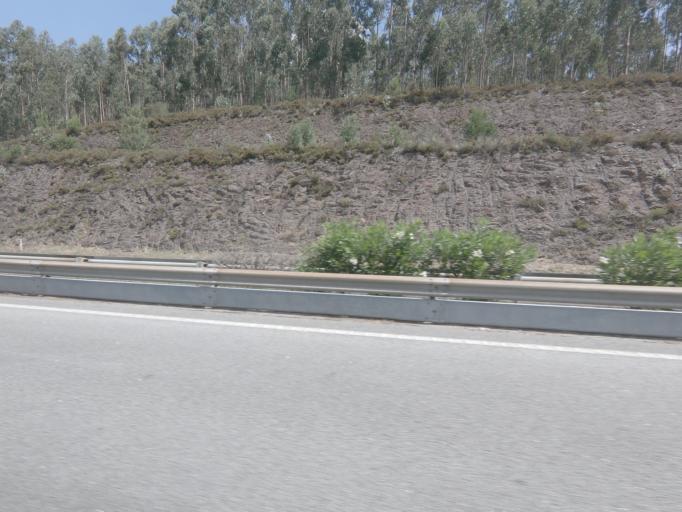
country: PT
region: Porto
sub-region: Paredes
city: Recarei
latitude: 41.1700
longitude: -8.4085
